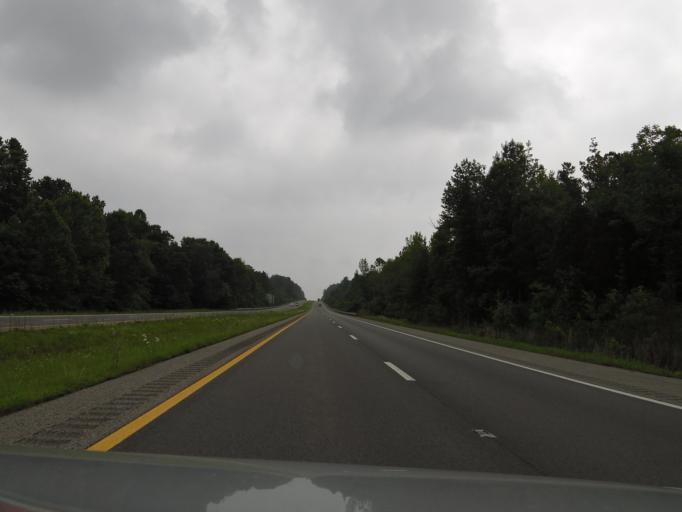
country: US
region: Kentucky
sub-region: Muhlenberg County
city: Morehead
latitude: 37.2485
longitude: -87.2322
